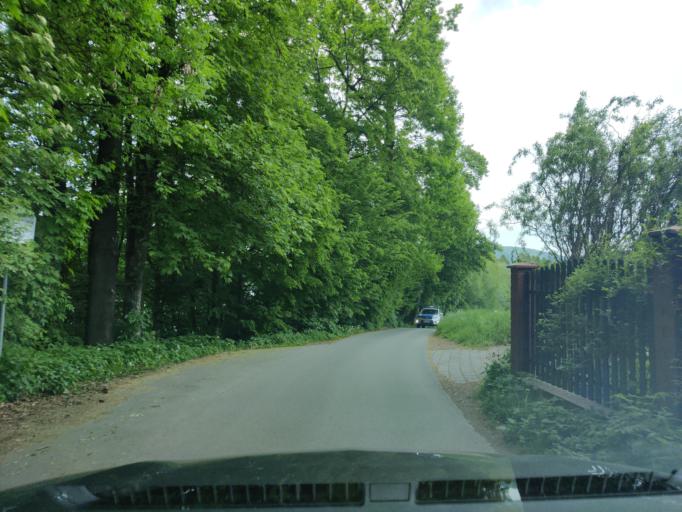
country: PL
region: Silesian Voivodeship
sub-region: Powiat zywiecki
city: Zywiec
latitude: 49.7129
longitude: 19.2062
